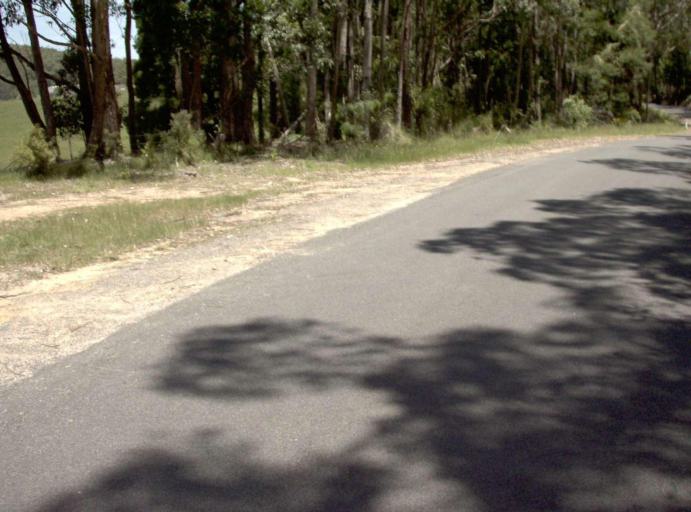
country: AU
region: New South Wales
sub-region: Bombala
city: Bombala
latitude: -37.5090
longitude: 148.9282
